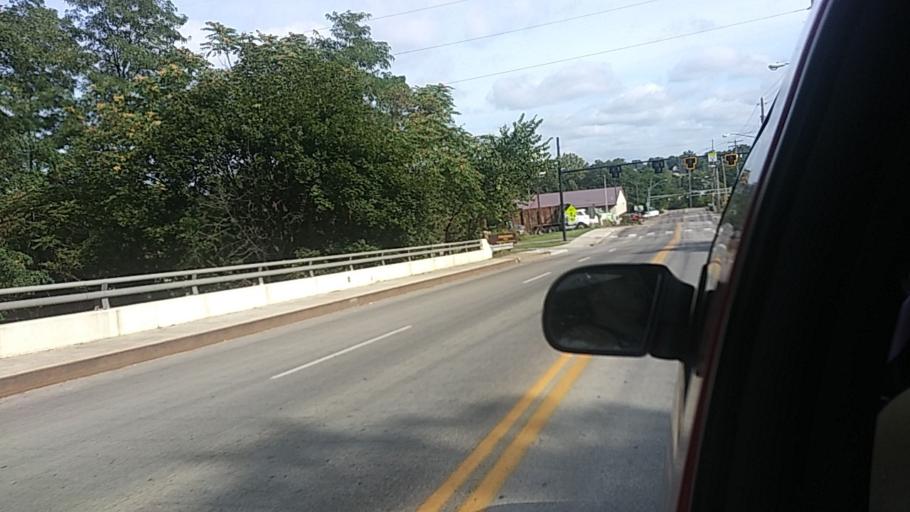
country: US
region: Ohio
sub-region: Summit County
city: Akron
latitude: 41.0835
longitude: -81.4904
